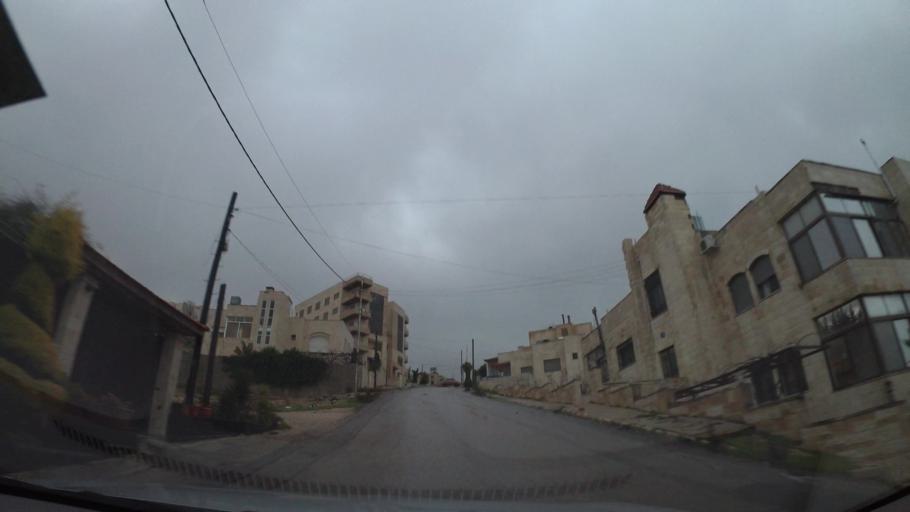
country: JO
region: Amman
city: Al Jubayhah
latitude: 32.0329
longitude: 35.8457
